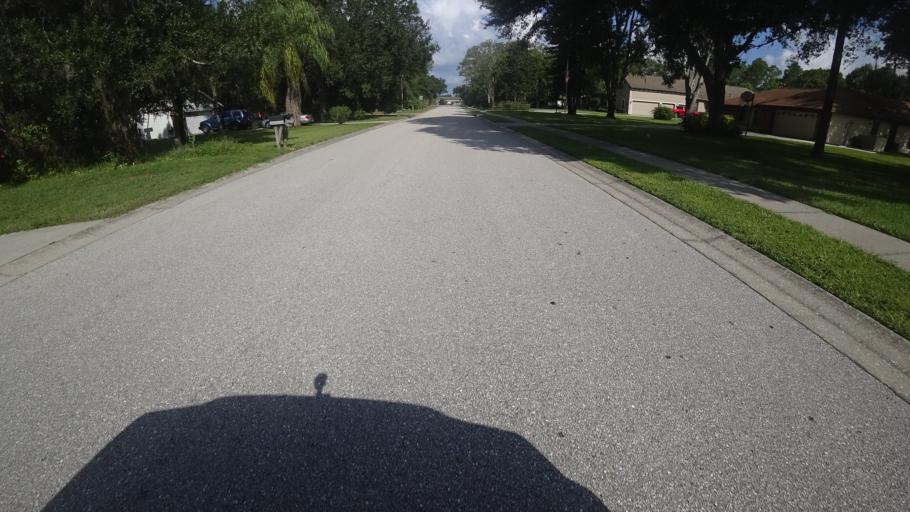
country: US
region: Florida
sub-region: Sarasota County
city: The Meadows
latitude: 27.4350
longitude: -82.4446
